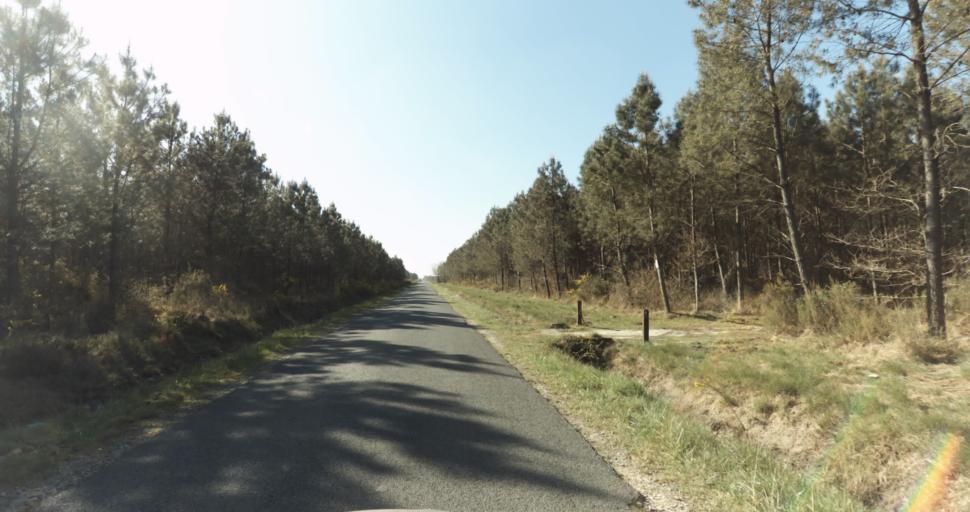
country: FR
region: Aquitaine
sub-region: Departement de la Gironde
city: Marcheprime
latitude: 44.7861
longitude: -0.8625
